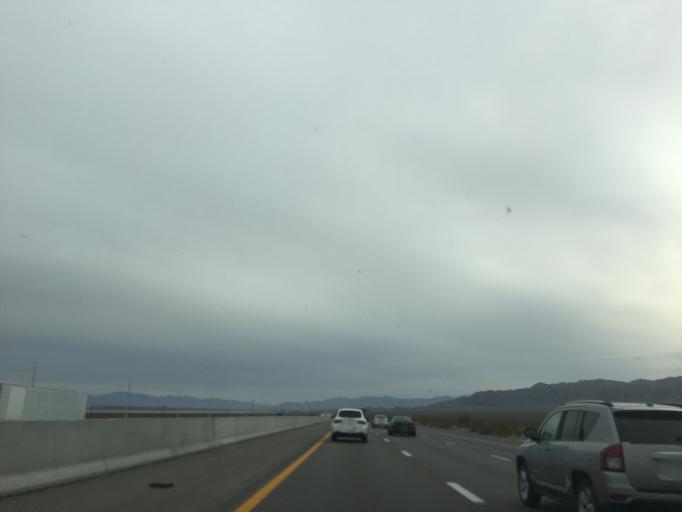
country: US
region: Nevada
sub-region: Clark County
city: Sandy Valley
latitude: 35.7298
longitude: -115.3601
